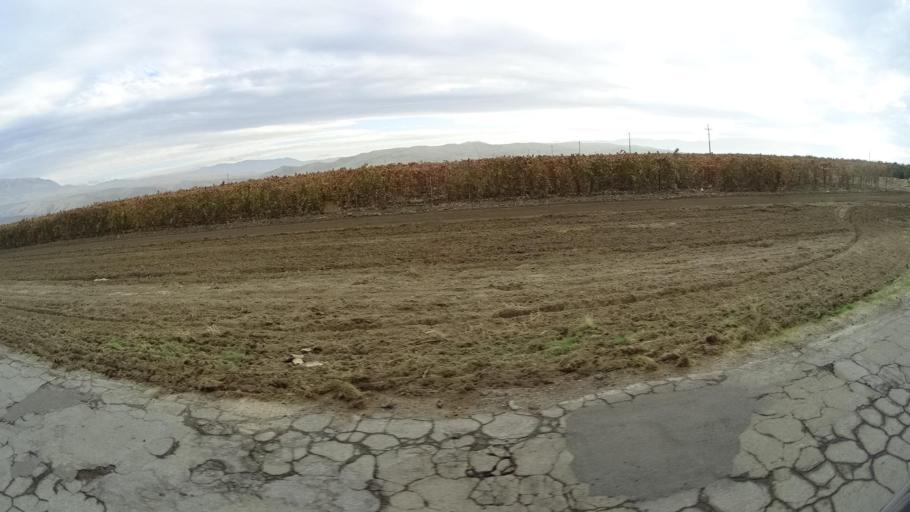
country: US
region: California
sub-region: Kern County
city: Arvin
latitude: 35.1511
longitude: -118.8225
